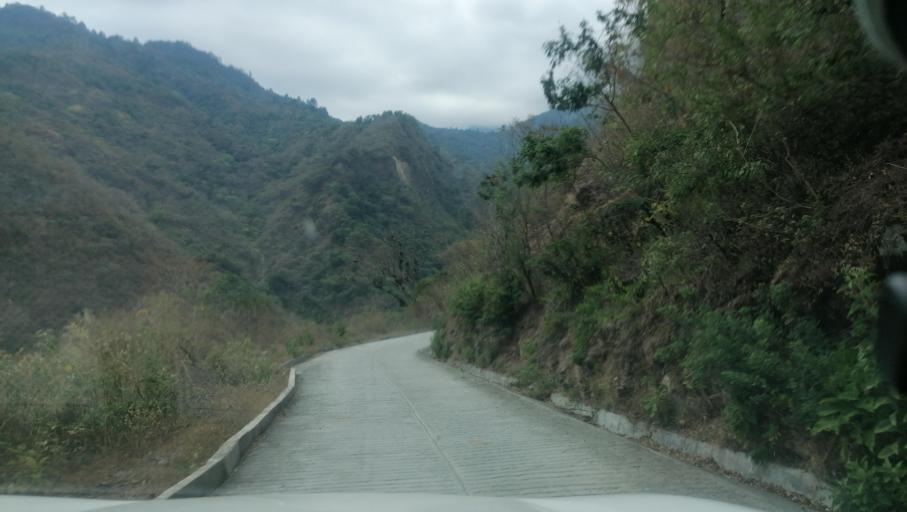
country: MX
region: Chiapas
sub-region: Cacahoatan
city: Benito Juarez
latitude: 15.1626
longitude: -92.1764
